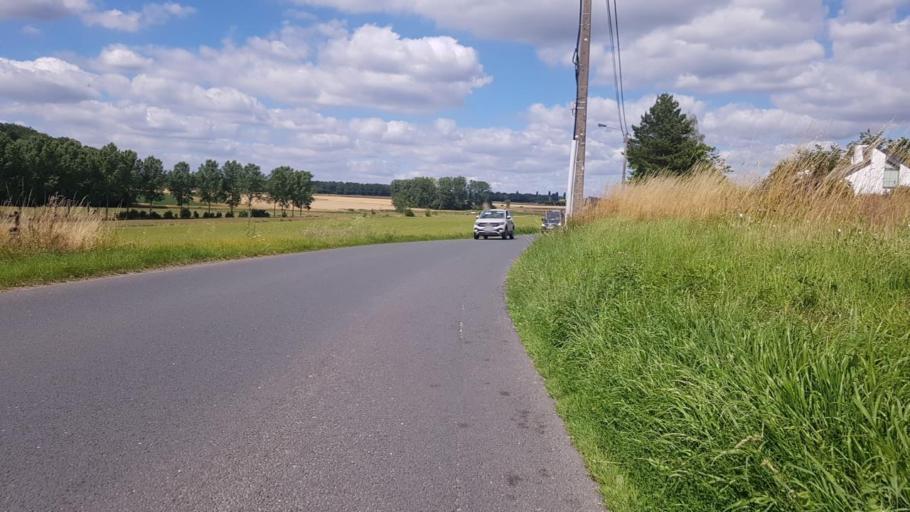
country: BE
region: Wallonia
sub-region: Province de Namur
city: Walcourt
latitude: 50.3286
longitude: 4.3809
